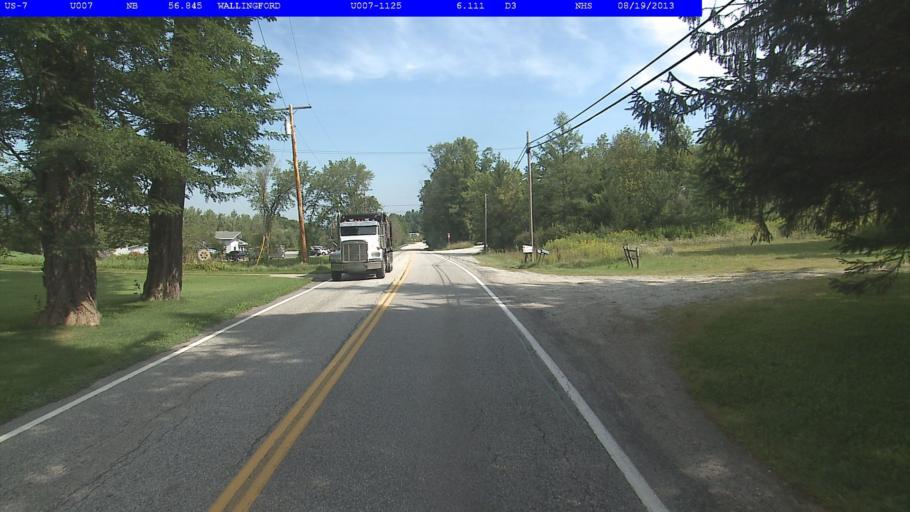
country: US
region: Vermont
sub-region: Rutland County
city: Rutland
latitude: 43.4805
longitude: -72.9744
